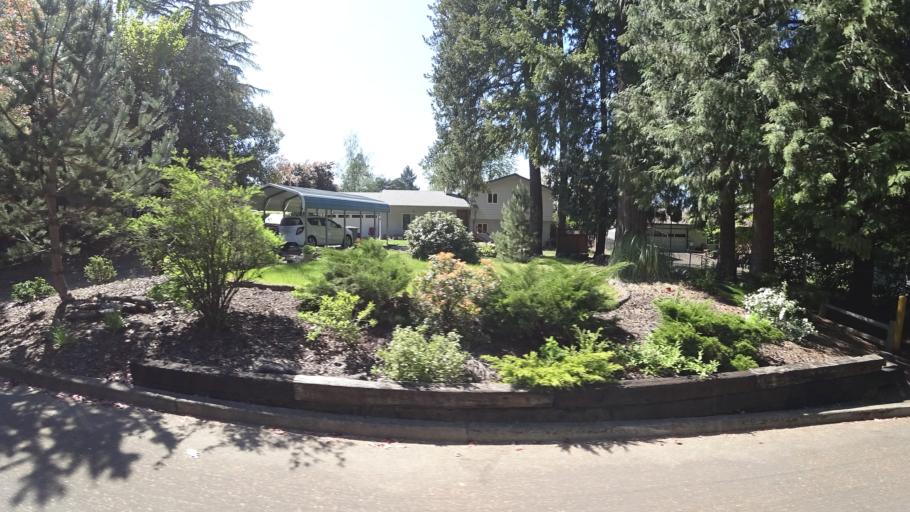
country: US
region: Oregon
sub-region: Washington County
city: Hillsboro
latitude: 45.5114
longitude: -122.9536
